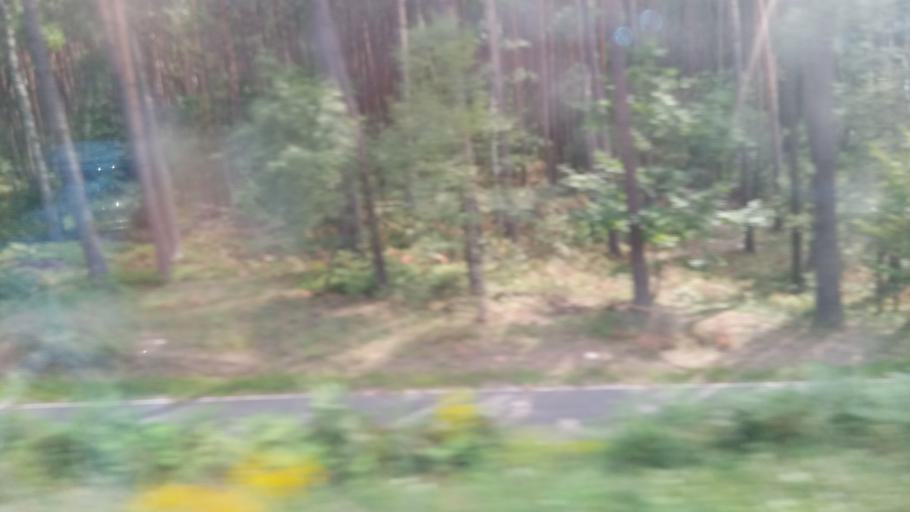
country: PL
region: Greater Poland Voivodeship
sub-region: Powiat pilski
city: Kaczory
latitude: 53.1111
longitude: 16.8522
